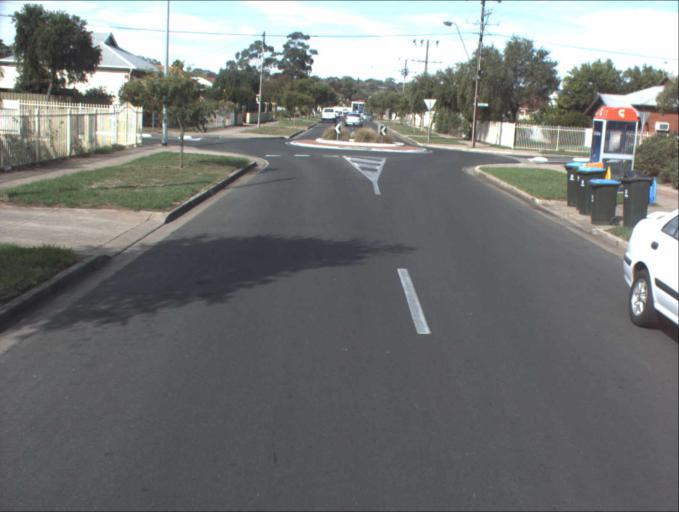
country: AU
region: South Australia
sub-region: Port Adelaide Enfield
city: Blair Athol
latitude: -34.8608
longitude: 138.5889
